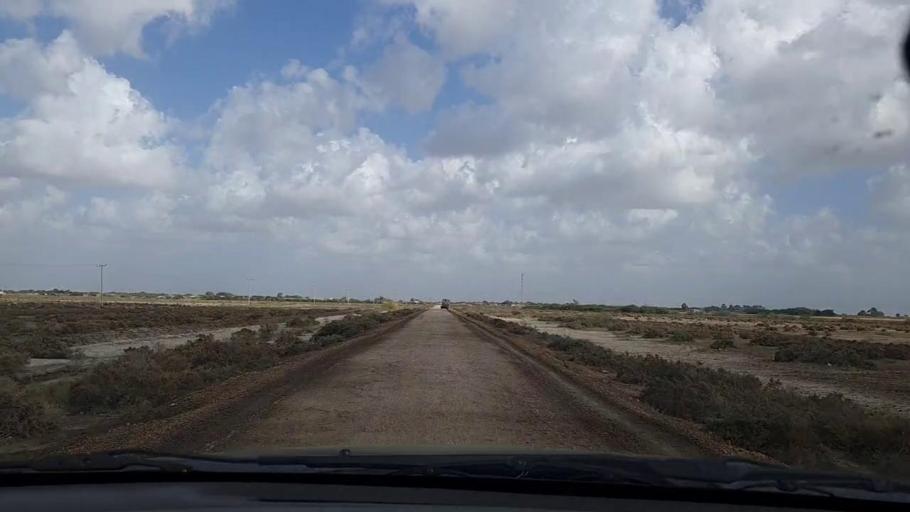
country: PK
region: Sindh
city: Keti Bandar
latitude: 24.1052
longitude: 67.5907
